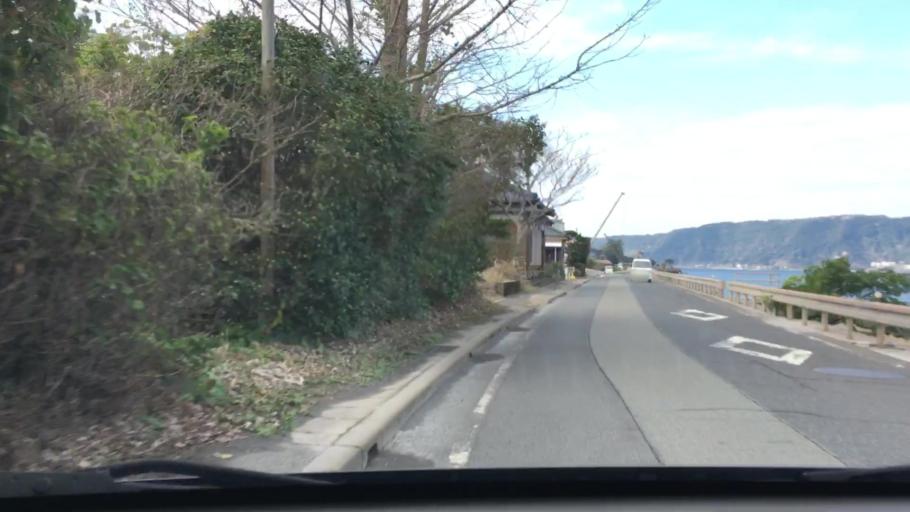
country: JP
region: Kagoshima
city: Kagoshima-shi
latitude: 31.6206
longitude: 130.6423
